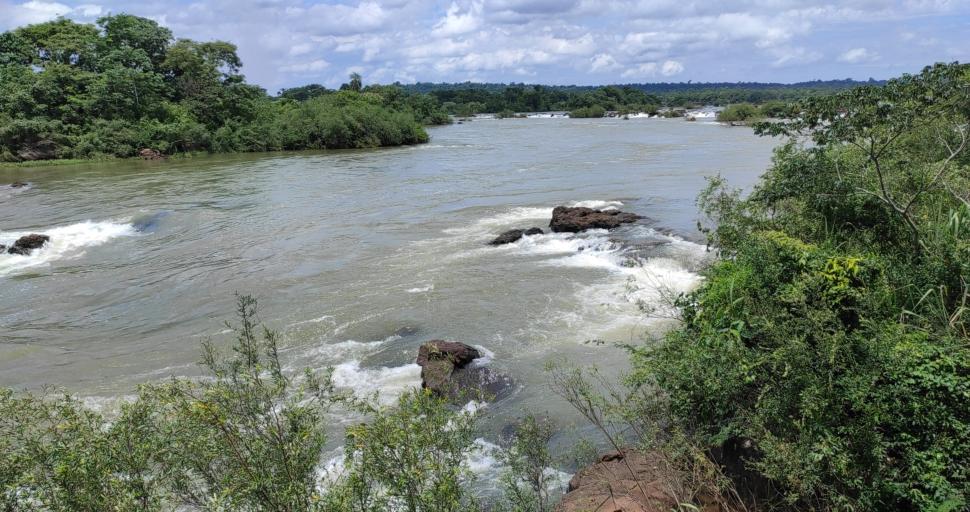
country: AR
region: Misiones
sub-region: Departamento de Iguazu
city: Puerto Iguazu
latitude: -25.6887
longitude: -54.4442
